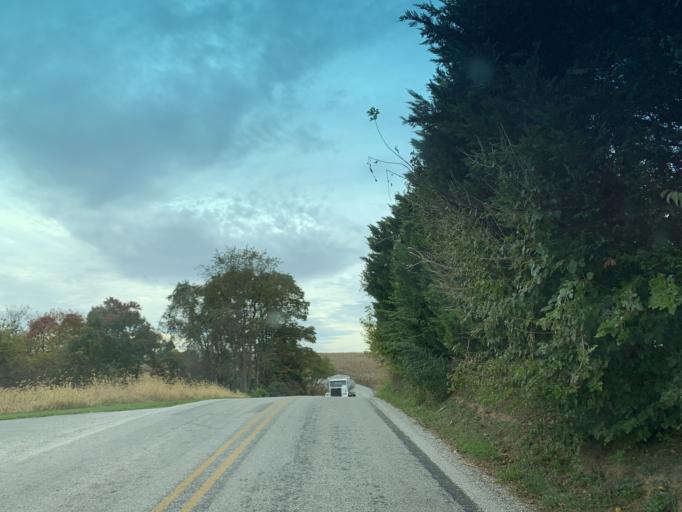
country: US
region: Pennsylvania
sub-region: York County
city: Stewartstown
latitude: 39.8093
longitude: -76.4890
